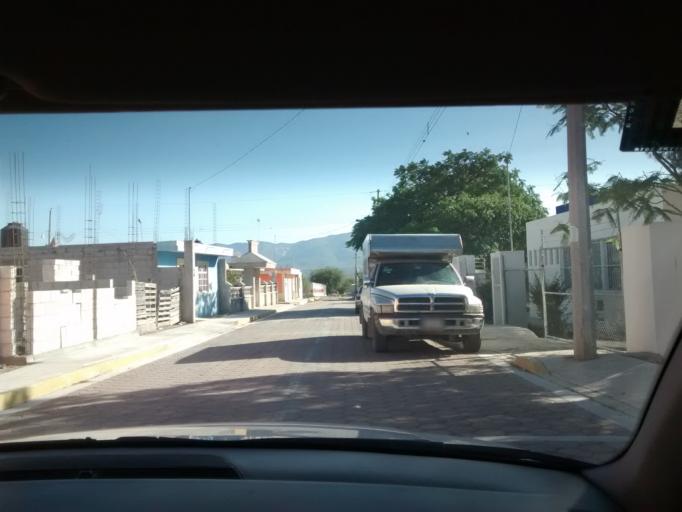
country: MX
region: Puebla
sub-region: Tepanco de Lopez
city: San Andres Cacaloapan
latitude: 18.5825
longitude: -97.5808
